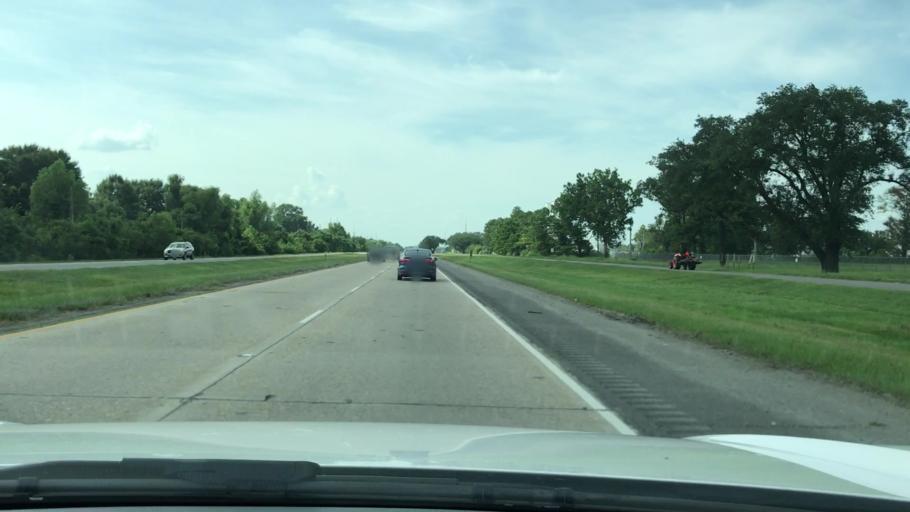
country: US
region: Louisiana
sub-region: Iberville Parish
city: Plaquemine
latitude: 30.3165
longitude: -91.2498
